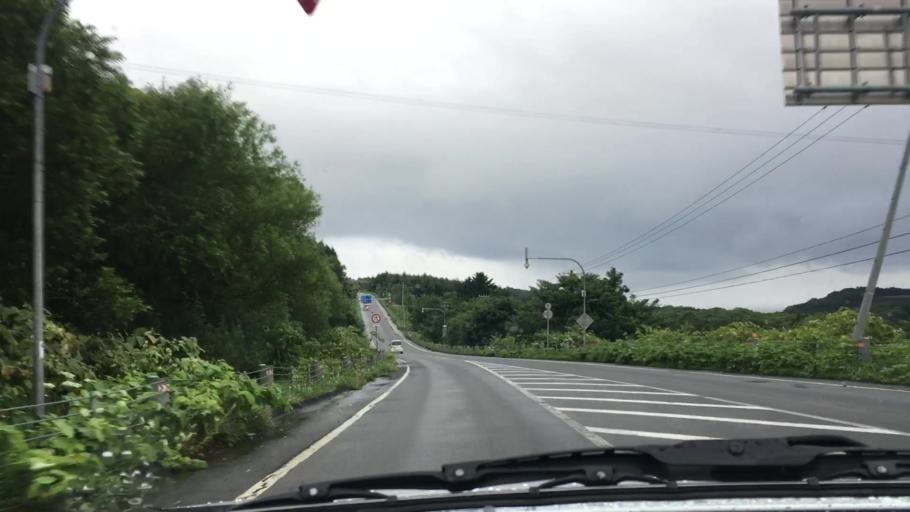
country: JP
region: Hokkaido
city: Niseko Town
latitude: 42.6050
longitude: 140.7267
